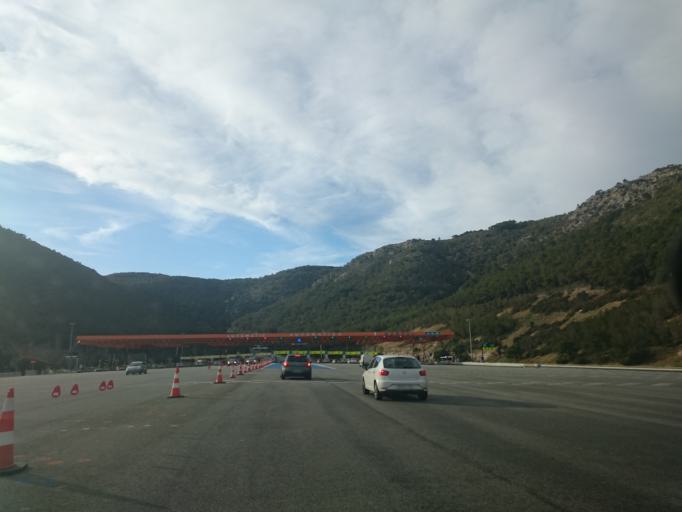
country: ES
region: Catalonia
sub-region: Provincia de Barcelona
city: Sitges
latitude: 41.2446
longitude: 1.8538
